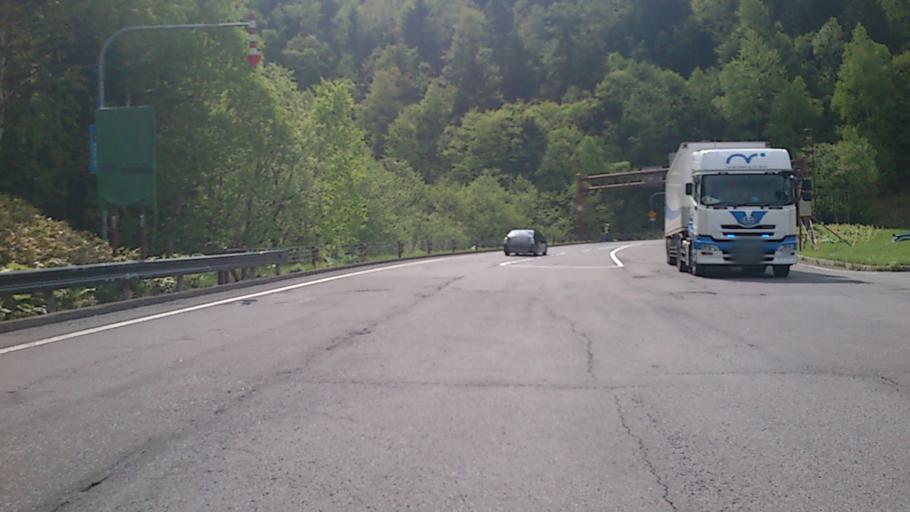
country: JP
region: Hokkaido
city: Kamikawa
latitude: 43.6810
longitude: 143.0367
